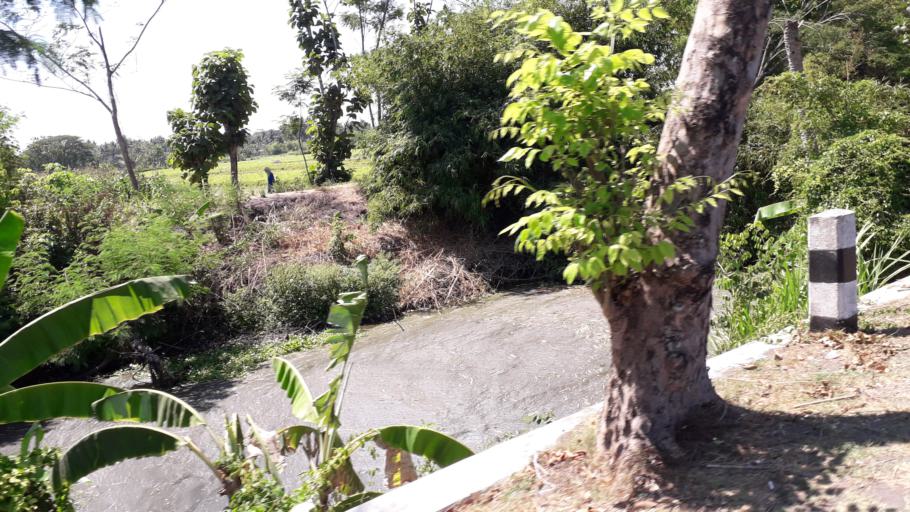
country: ID
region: Daerah Istimewa Yogyakarta
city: Pundong
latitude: -7.9465
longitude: 110.3293
